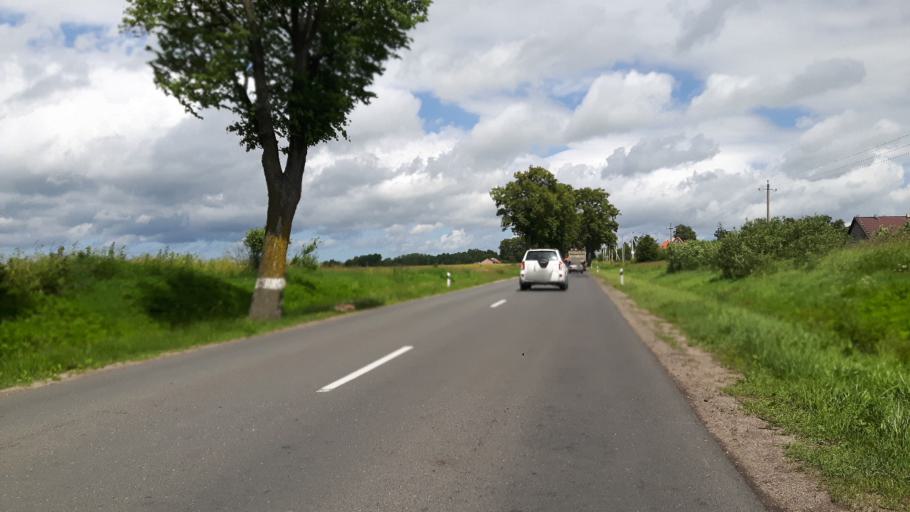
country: RU
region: Kaliningrad
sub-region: Gorod Kaliningrad
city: Kaliningrad
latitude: 54.8115
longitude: 20.4165
